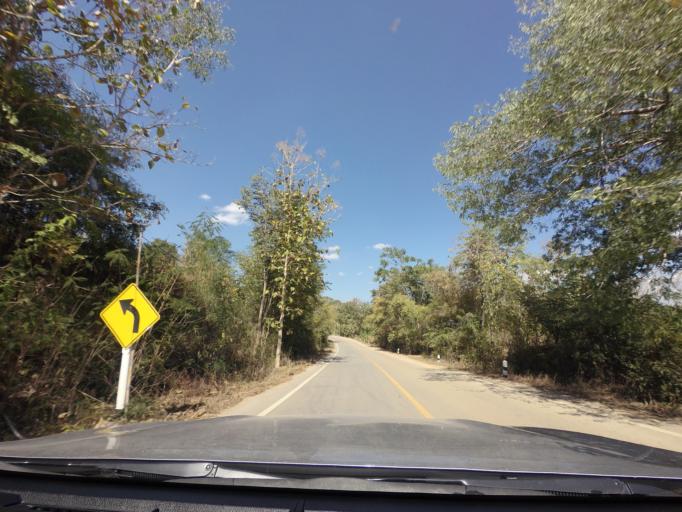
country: TH
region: Lampang
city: Chae Hom
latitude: 18.5341
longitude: 99.6427
